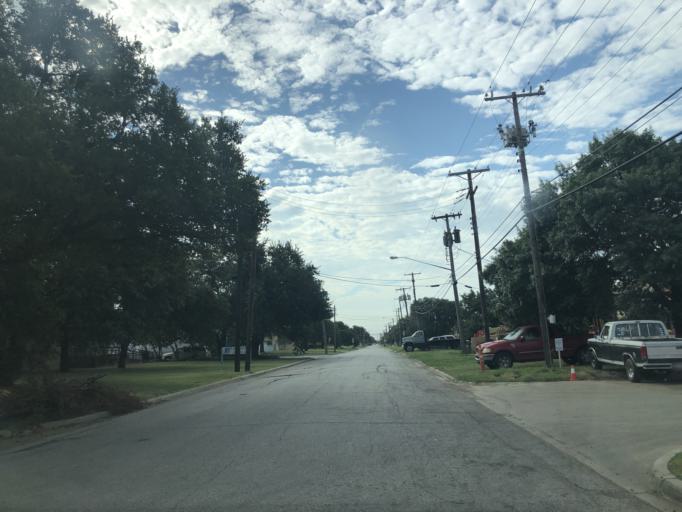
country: US
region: Texas
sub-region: Dallas County
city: Irving
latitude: 32.8211
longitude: -96.8879
